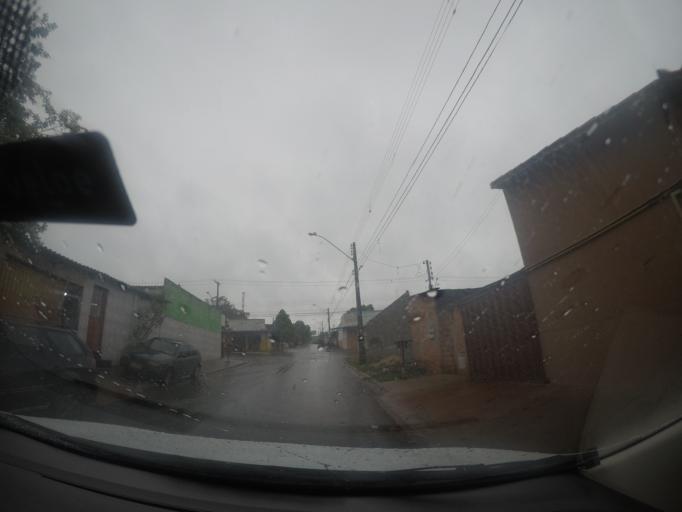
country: BR
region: Goias
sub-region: Goiania
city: Goiania
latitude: -16.6004
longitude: -49.3284
